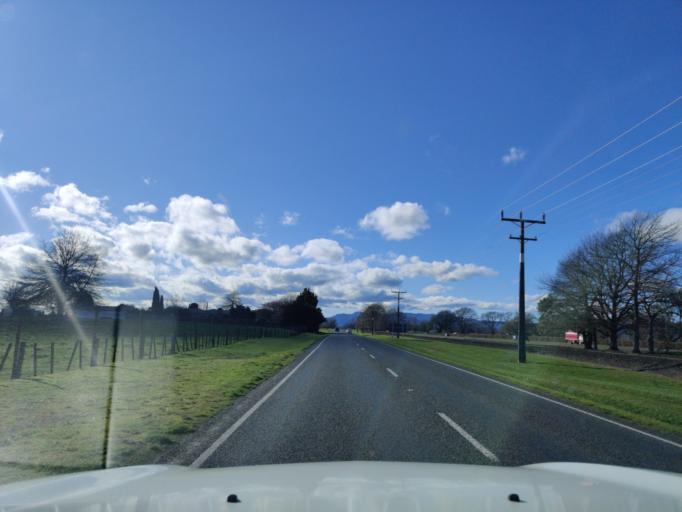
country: NZ
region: Waikato
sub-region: Matamata-Piako District
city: Matamata
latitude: -37.8476
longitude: 175.7603
